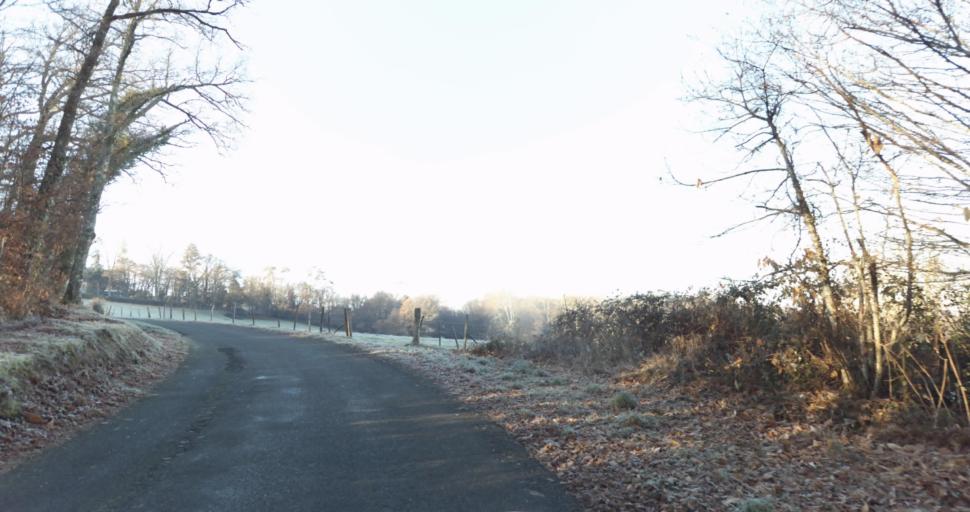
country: FR
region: Limousin
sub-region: Departement de la Haute-Vienne
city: Aixe-sur-Vienne
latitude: 45.8245
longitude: 1.1396
